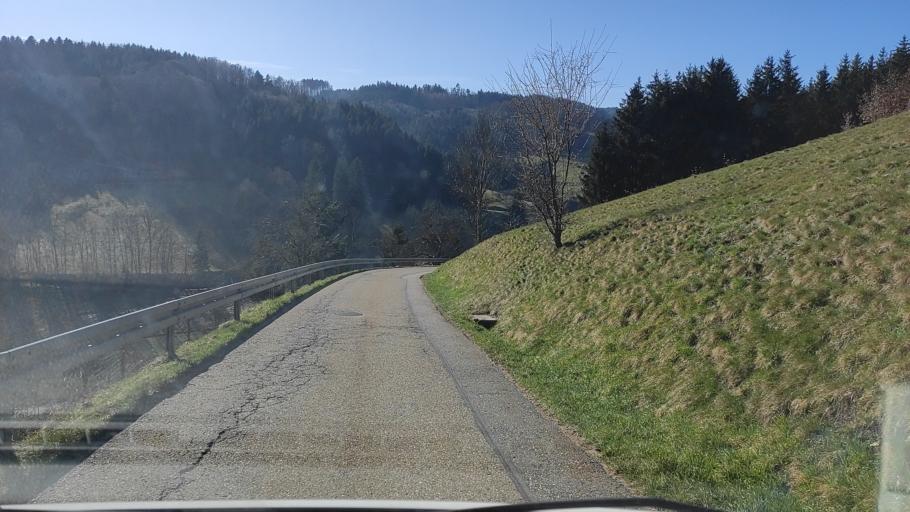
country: DE
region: Baden-Wuerttemberg
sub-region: Freiburg Region
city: Elzach
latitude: 48.1629
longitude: 8.0258
